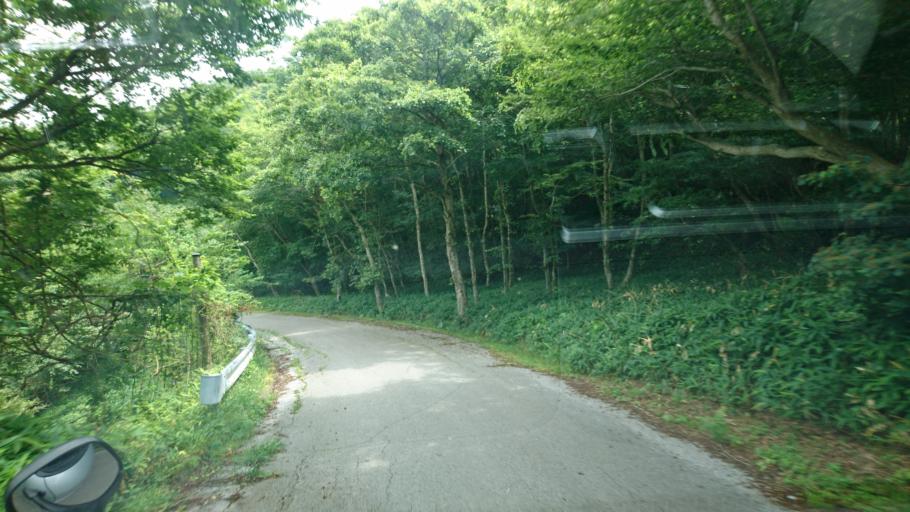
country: JP
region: Iwate
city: Ofunato
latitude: 39.1337
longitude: 141.7559
